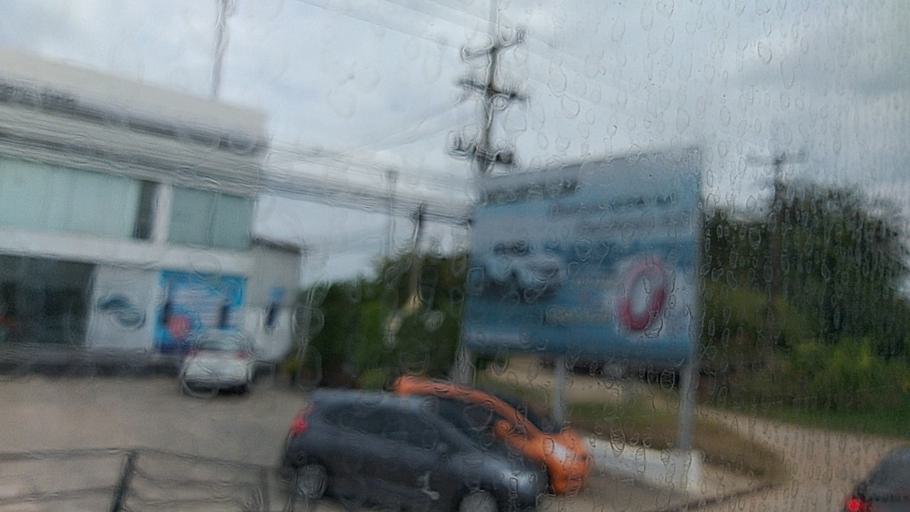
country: TH
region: Maha Sarakham
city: Maha Sarakham
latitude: 16.1651
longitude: 103.3351
